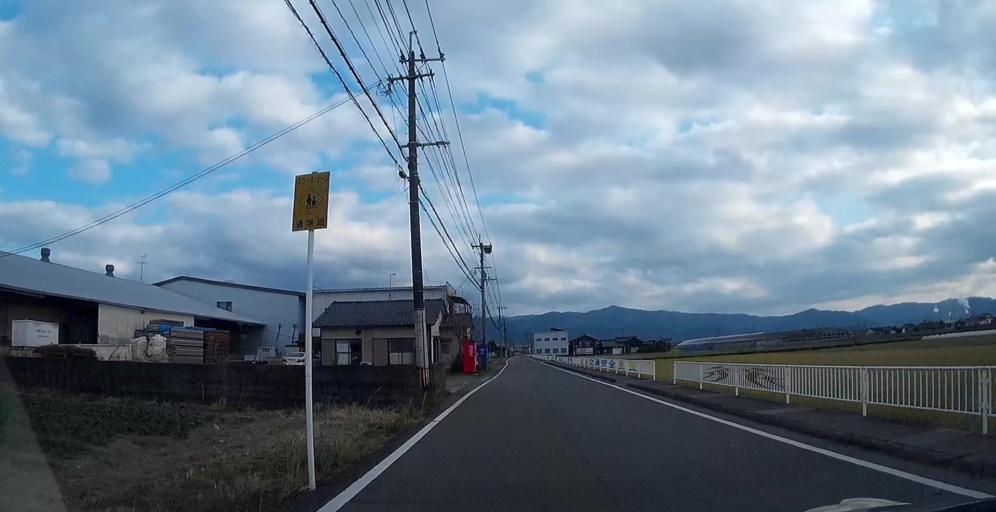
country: JP
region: Kumamoto
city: Yatsushiro
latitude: 32.5446
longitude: 130.6199
